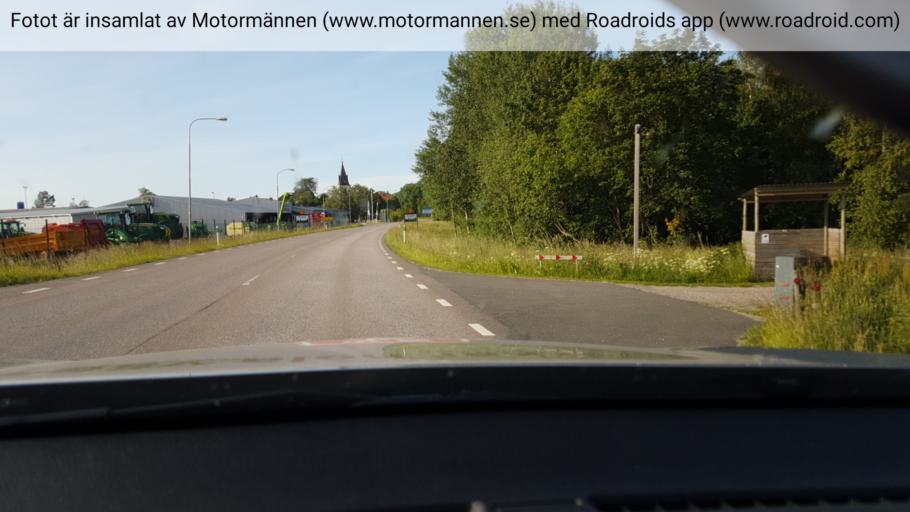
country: SE
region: Vaestra Goetaland
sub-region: Falkopings Kommun
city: Falkoeping
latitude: 58.0173
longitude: 13.5719
